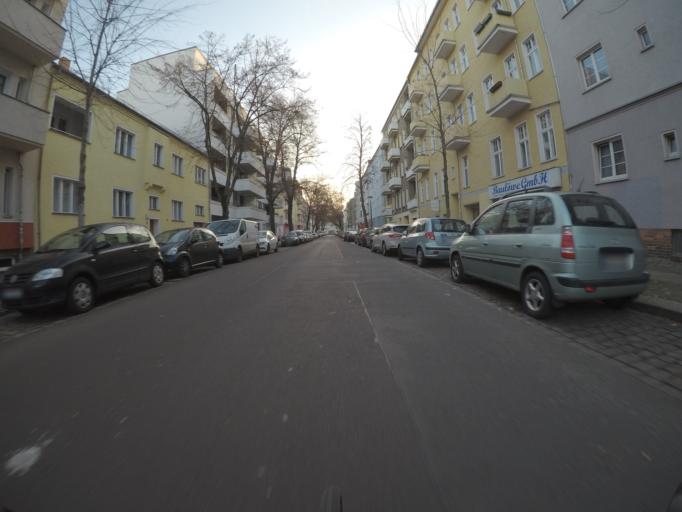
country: DE
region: Berlin
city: Rummelsburg
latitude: 52.5035
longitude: 13.4902
